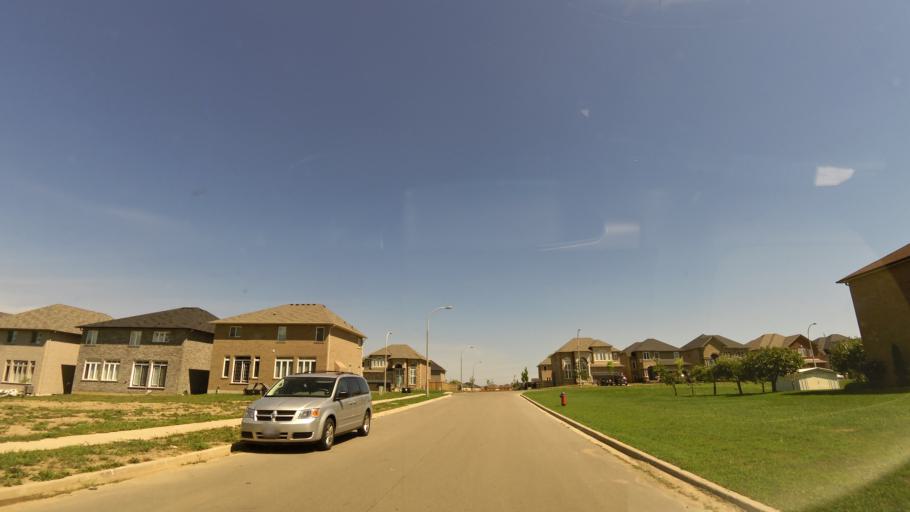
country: CA
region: Ontario
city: Ancaster
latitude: 43.2140
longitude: -79.9468
